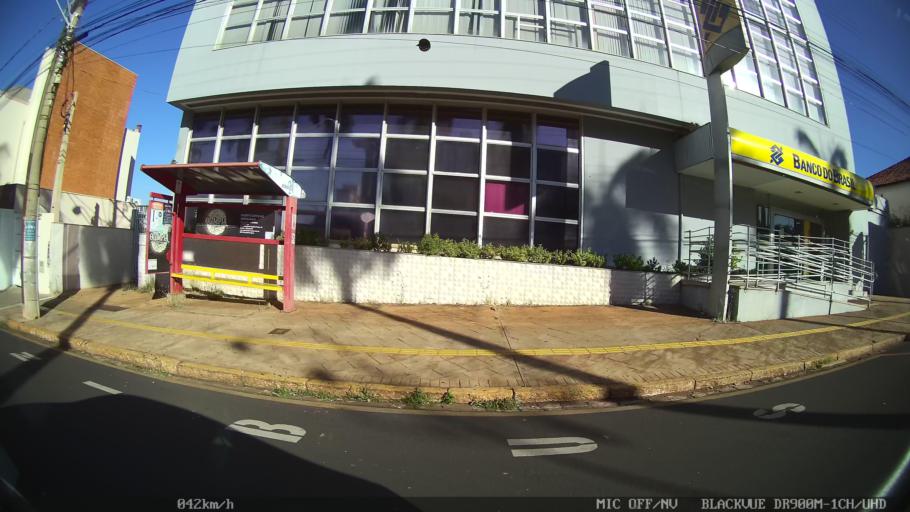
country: BR
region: Sao Paulo
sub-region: Olimpia
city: Olimpia
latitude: -20.7388
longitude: -48.9151
